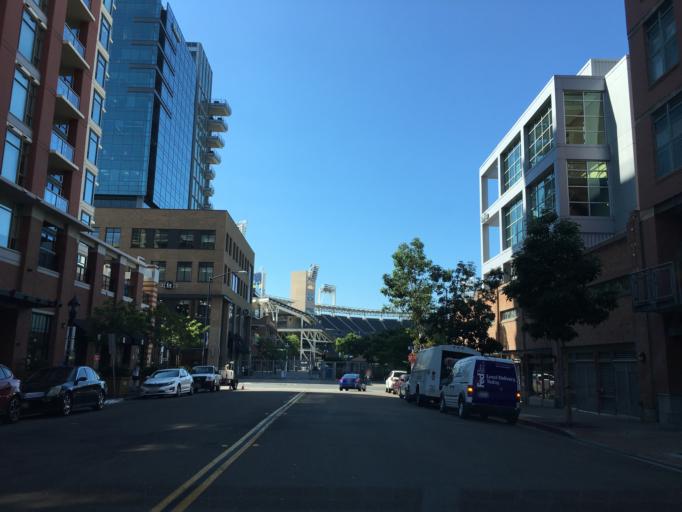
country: US
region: California
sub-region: San Diego County
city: San Diego
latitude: 32.7100
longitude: -117.1566
